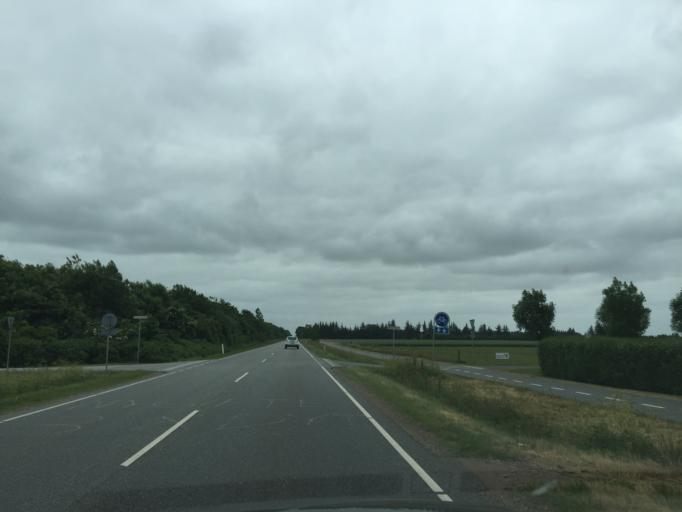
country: DK
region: South Denmark
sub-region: Esbjerg Kommune
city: Ribe
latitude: 55.3108
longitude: 8.7487
